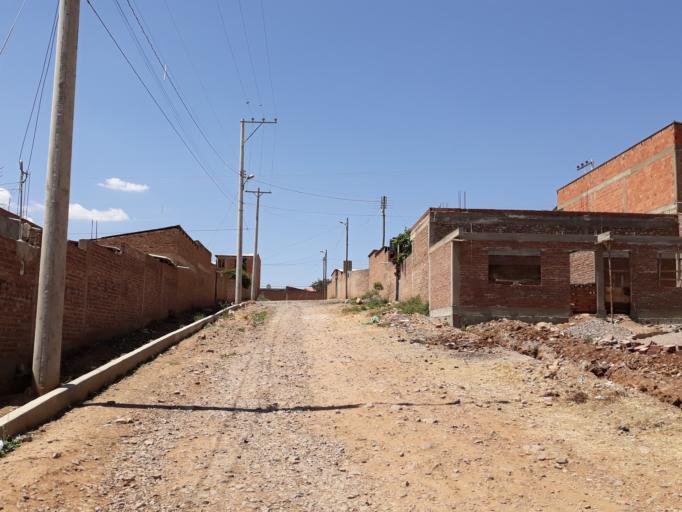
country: BO
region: Cochabamba
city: Cochabamba
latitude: -17.4613
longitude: -66.1364
